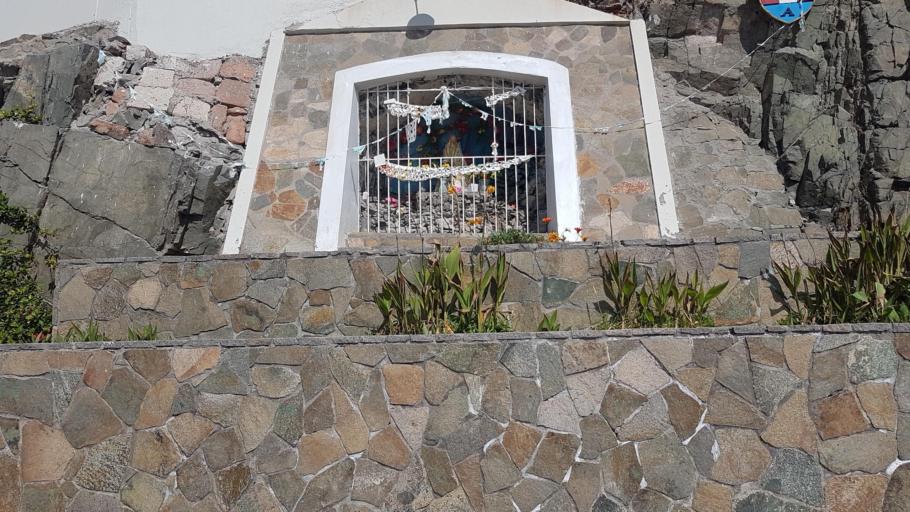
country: PE
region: Arequipa
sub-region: Provincia de Islay
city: Mollendo
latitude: -17.0319
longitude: -72.0147
